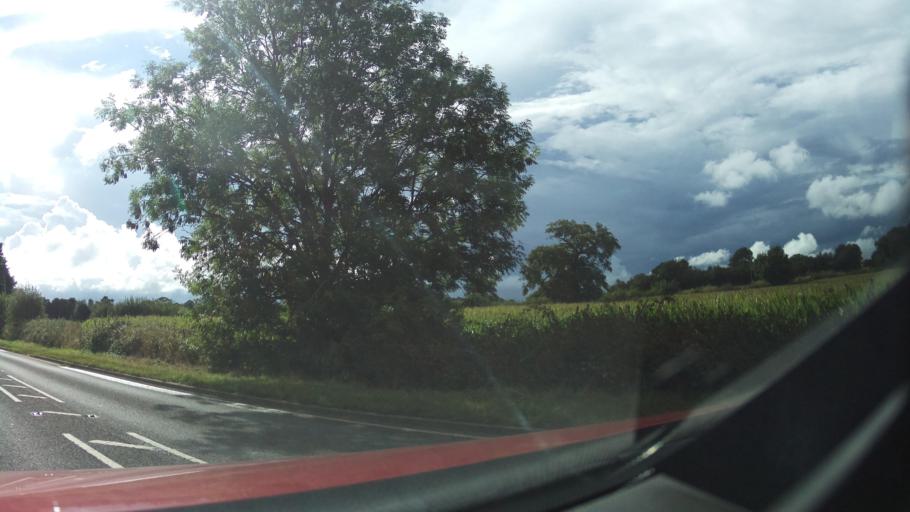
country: GB
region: England
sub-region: Shropshire
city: Shifnal
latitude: 52.6510
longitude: -2.4006
